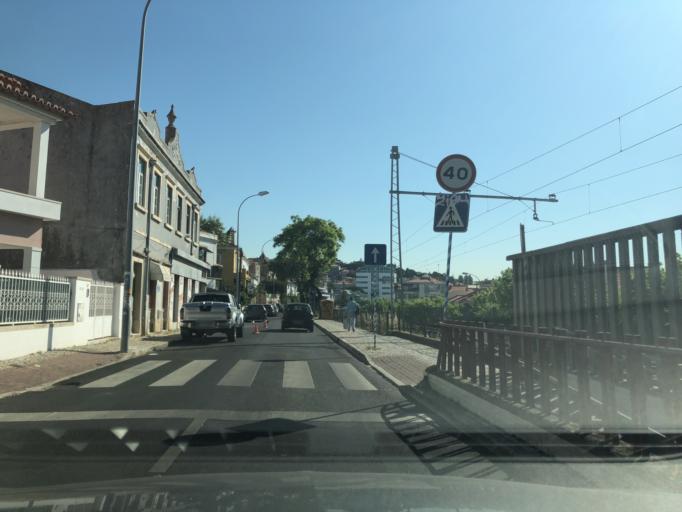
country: PT
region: Lisbon
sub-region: Oeiras
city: Paco de Arcos
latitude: 38.6957
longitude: -9.2960
